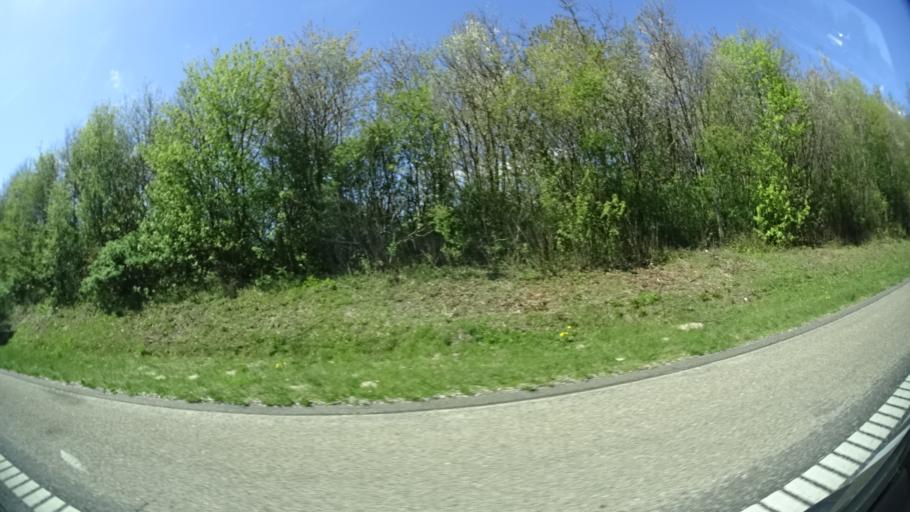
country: DK
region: Central Jutland
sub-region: Arhus Kommune
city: Framlev
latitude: 56.1679
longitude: 10.0520
